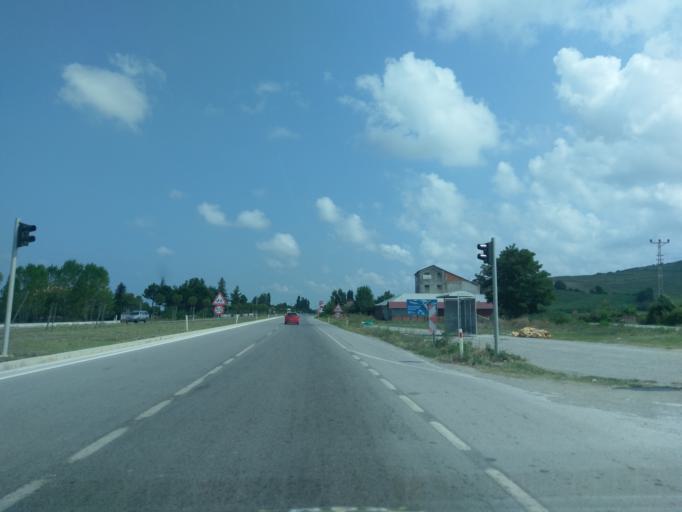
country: TR
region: Samsun
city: Alacam
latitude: 41.6107
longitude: 35.6998
